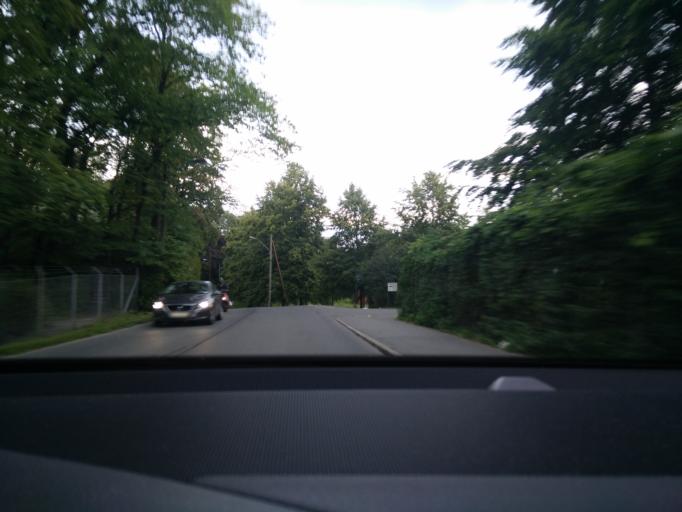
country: NO
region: Oslo
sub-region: Oslo
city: Sjolyststranda
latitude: 59.9101
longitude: 10.6803
